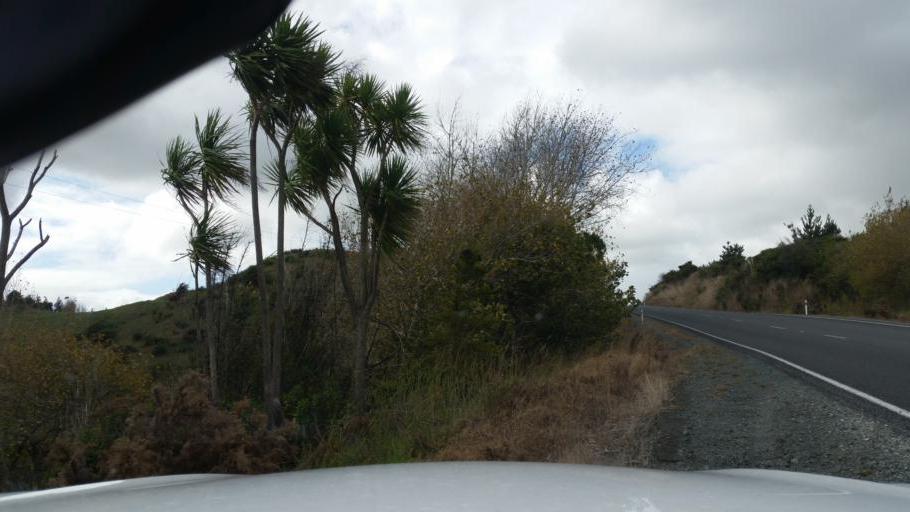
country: NZ
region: Northland
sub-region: Whangarei
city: Ruakaka
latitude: -36.0801
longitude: 174.2398
